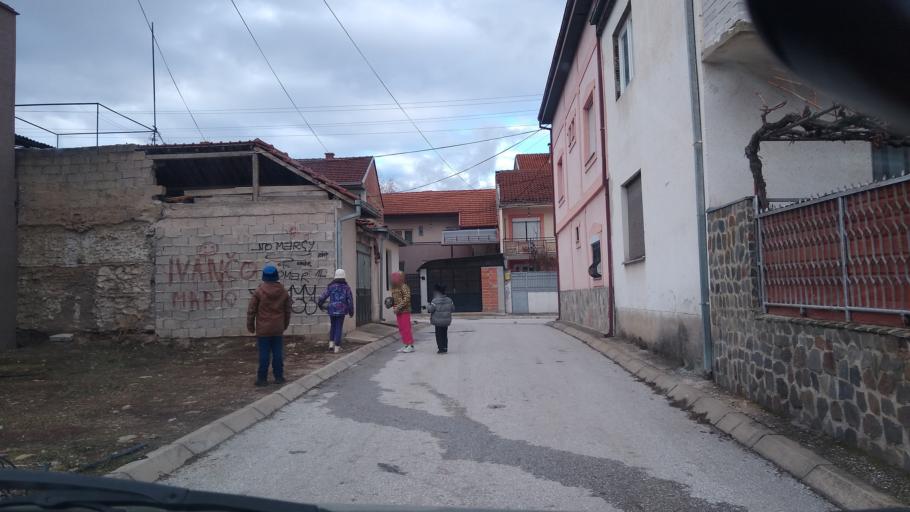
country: MK
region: Bitola
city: Bitola
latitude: 41.0315
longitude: 21.3178
